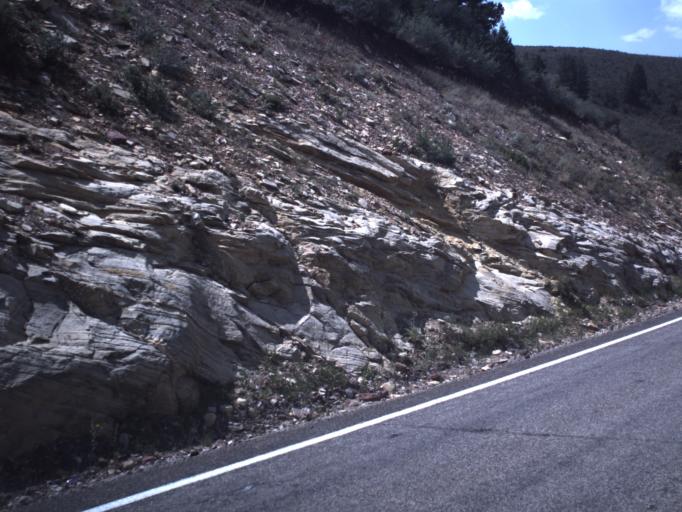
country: US
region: Utah
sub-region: Uintah County
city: Vernal
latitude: 40.6611
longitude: -109.4820
